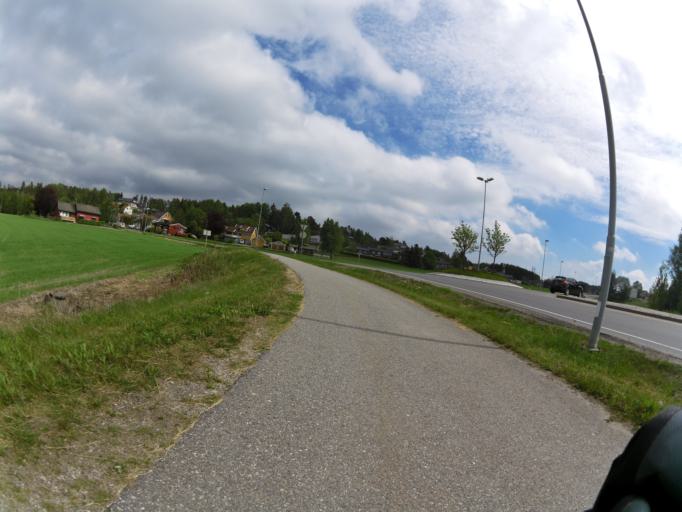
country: NO
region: Ostfold
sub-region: Rade
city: Karlshus
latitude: 59.3453
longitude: 10.9303
